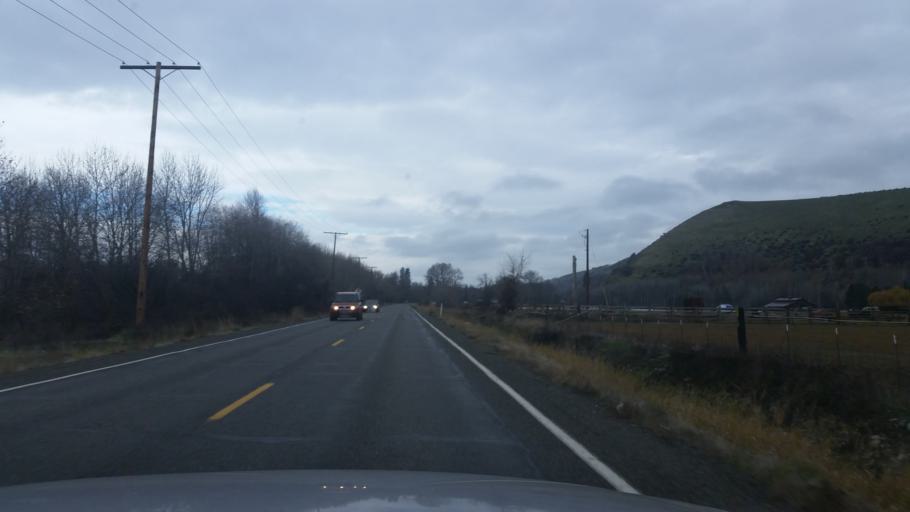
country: US
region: Washington
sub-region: Kittitas County
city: Ellensburg
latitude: 47.0542
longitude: -120.6395
